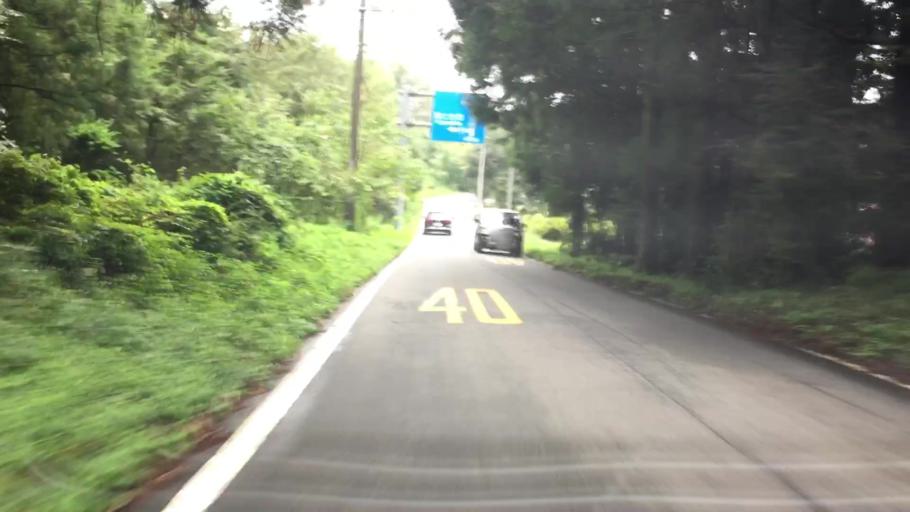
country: JP
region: Shizuoka
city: Fujinomiya
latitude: 35.3582
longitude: 138.5917
